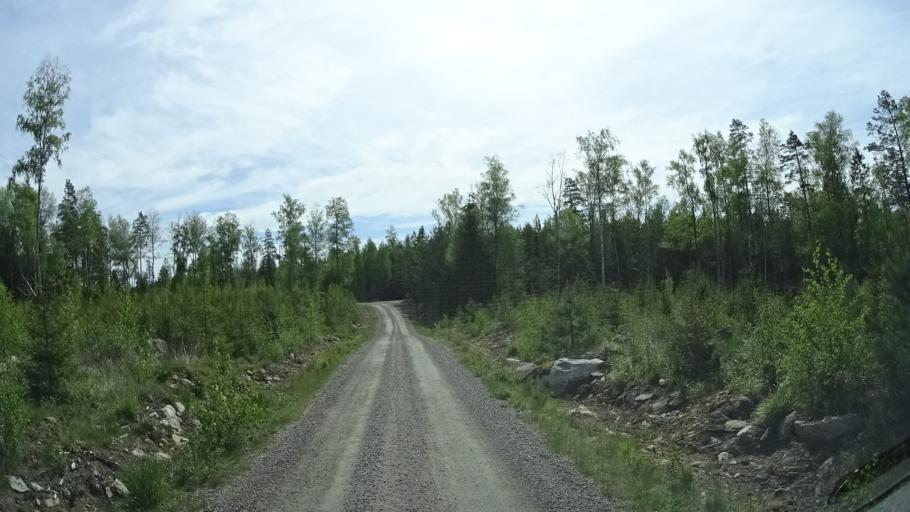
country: SE
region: OEstergoetland
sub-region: Finspangs Kommun
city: Finspang
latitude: 58.7792
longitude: 15.8622
